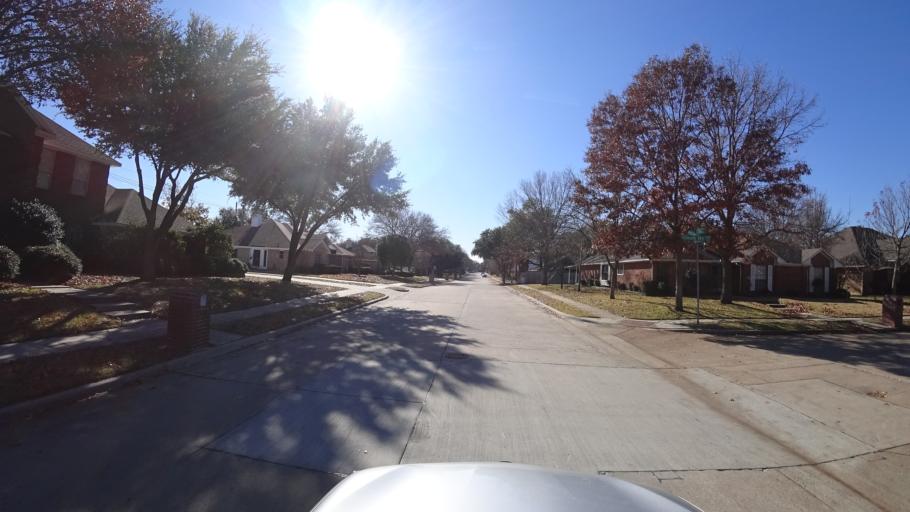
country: US
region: Texas
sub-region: Denton County
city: Lewisville
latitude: 33.0182
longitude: -97.0231
